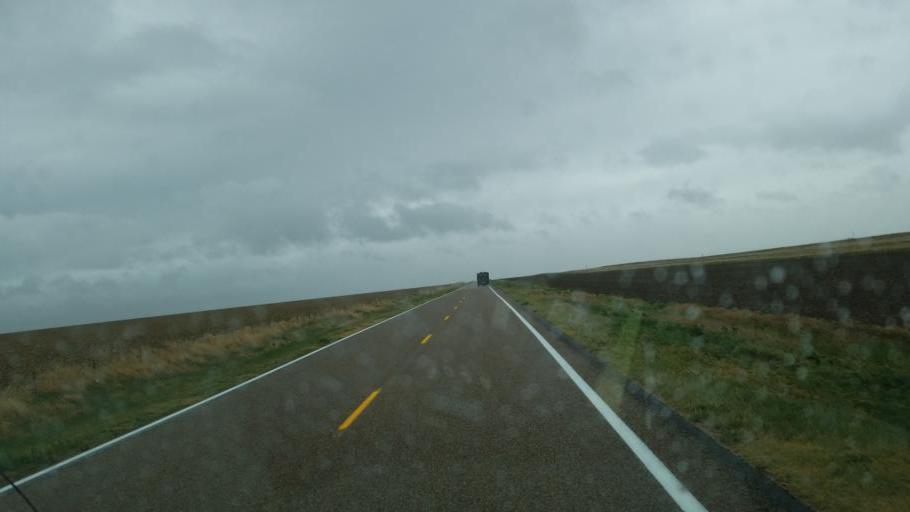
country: US
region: Colorado
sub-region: Cheyenne County
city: Cheyenne Wells
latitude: 38.8521
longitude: -102.2278
